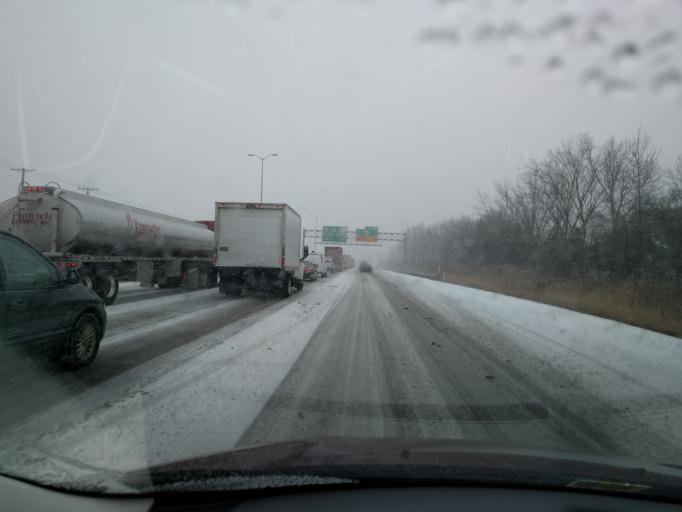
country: US
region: Wisconsin
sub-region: Waukesha County
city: Menomonee Falls
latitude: 43.1653
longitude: -88.0715
